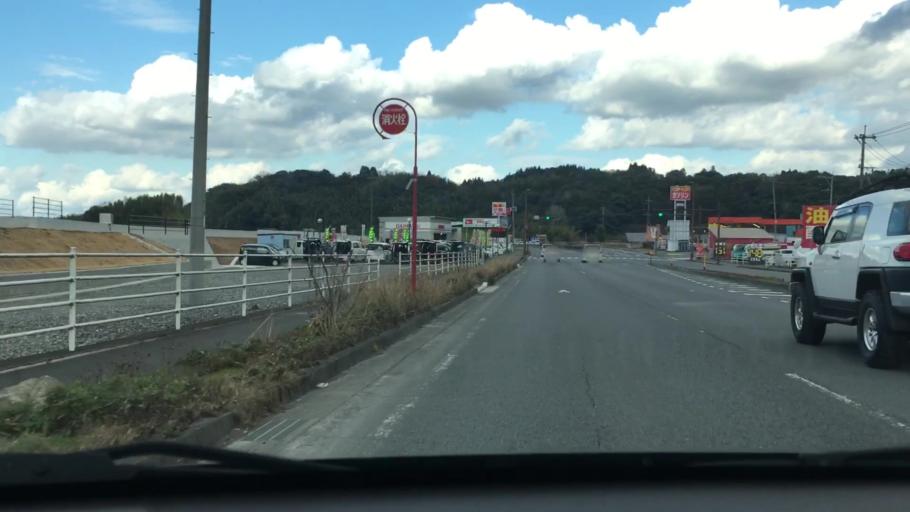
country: JP
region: Oita
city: Oita
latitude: 33.1307
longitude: 131.6587
